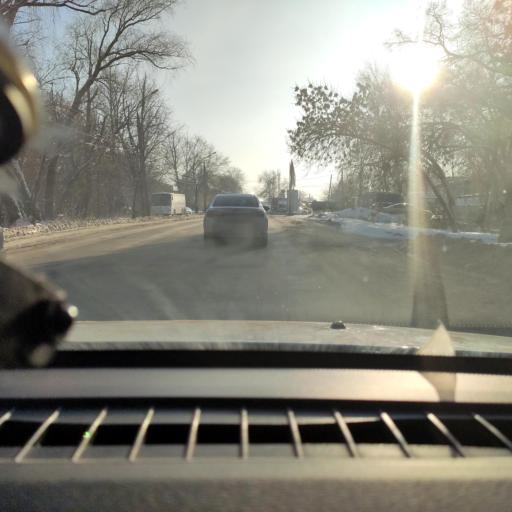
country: RU
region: Samara
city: Samara
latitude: 53.1074
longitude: 50.0716
